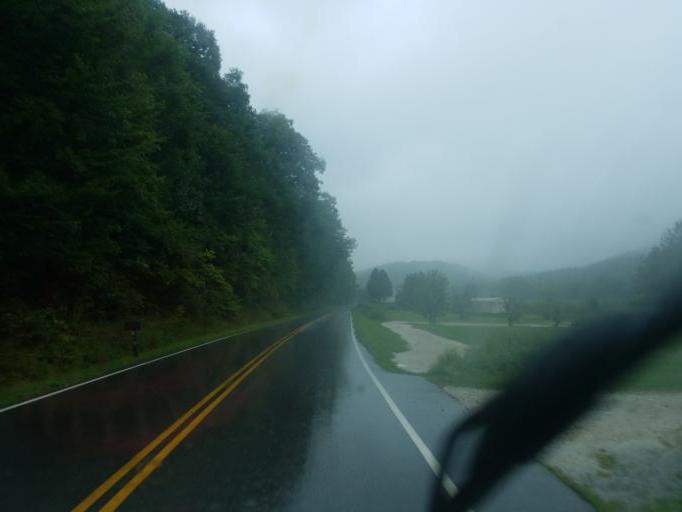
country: US
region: Kentucky
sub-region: Carter County
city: Grayson
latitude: 38.4698
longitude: -83.0440
